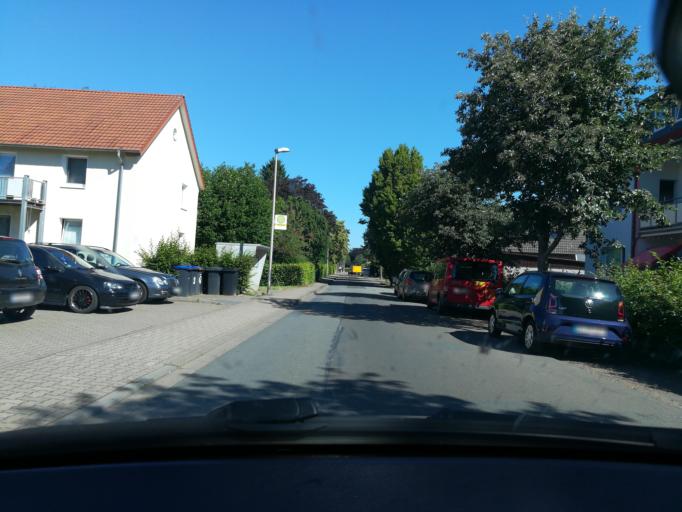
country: DE
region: North Rhine-Westphalia
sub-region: Regierungsbezirk Detmold
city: Minden
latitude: 52.3143
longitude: 8.9331
